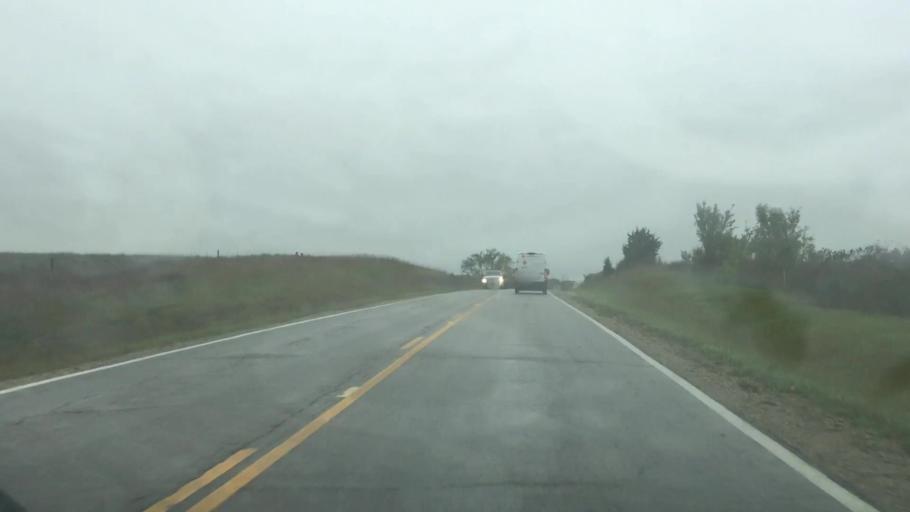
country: US
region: Kansas
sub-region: Anderson County
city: Garnett
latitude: 38.2404
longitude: -95.2480
